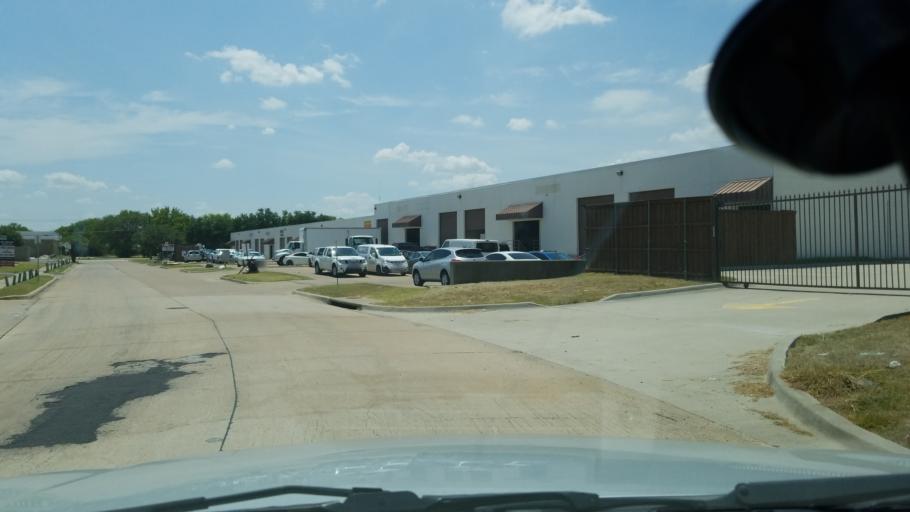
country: US
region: Texas
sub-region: Dallas County
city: Irving
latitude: 32.8235
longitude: -96.9917
